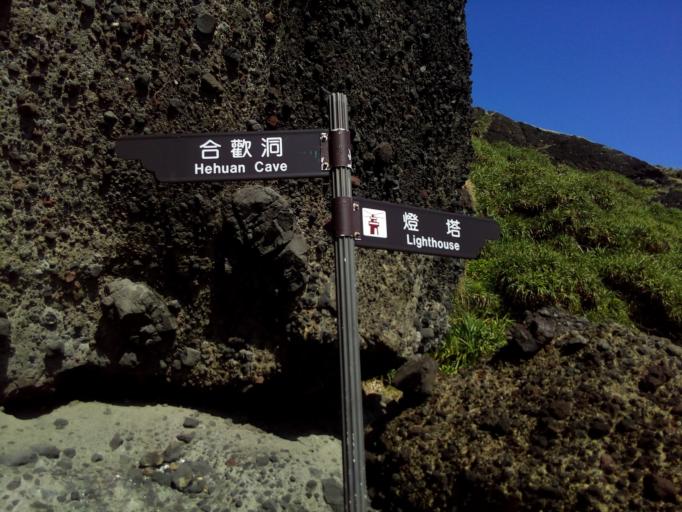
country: TW
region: Taiwan
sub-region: Taitung
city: Taitung
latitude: 23.1257
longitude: 121.4211
